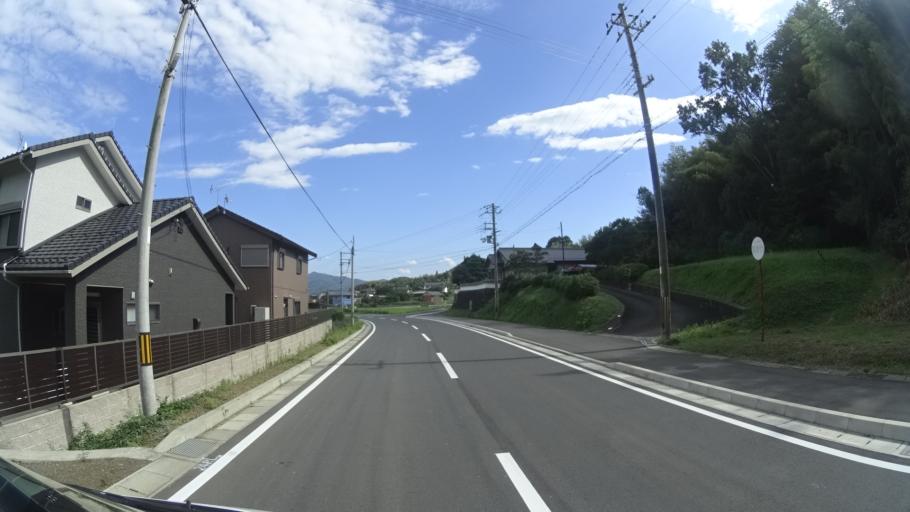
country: JP
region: Kyoto
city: Fukuchiyama
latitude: 35.3326
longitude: 135.1718
